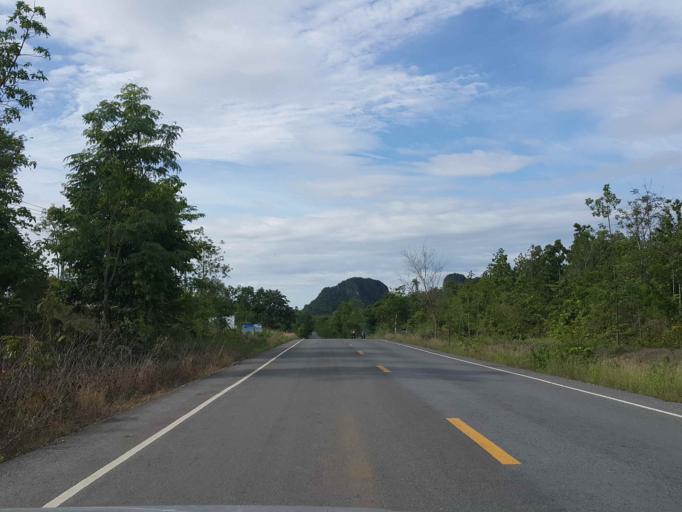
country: TH
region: Sukhothai
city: Thung Saliam
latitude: 17.2969
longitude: 99.5270
